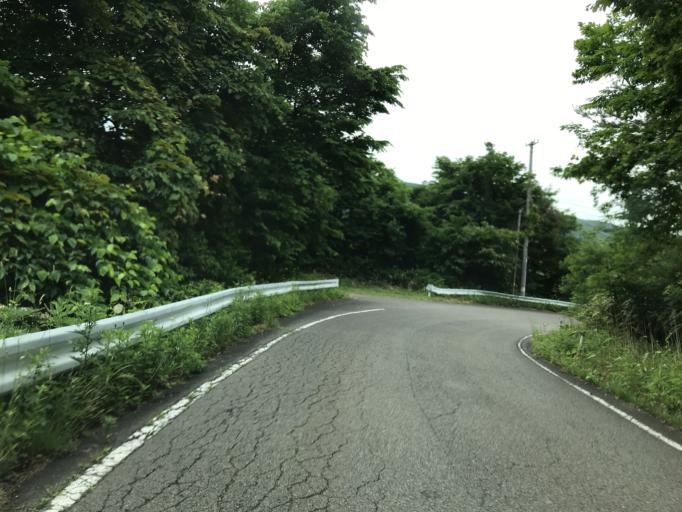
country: JP
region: Fukushima
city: Funehikimachi-funehiki
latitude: 37.4201
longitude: 140.7341
